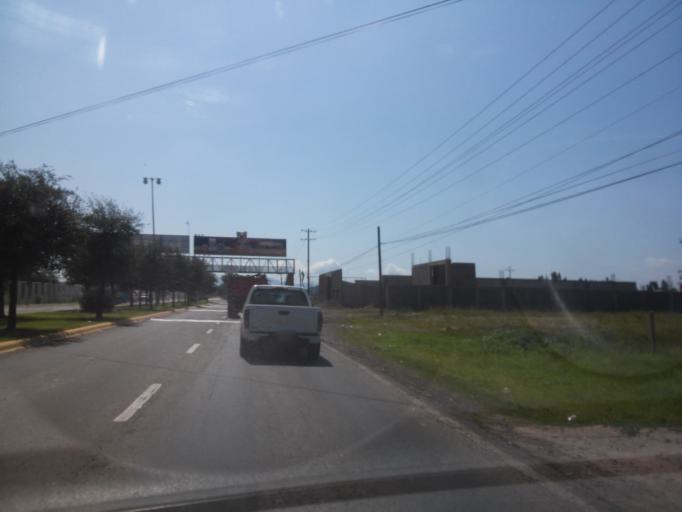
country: MX
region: Durango
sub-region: Durango
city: Sebastian Lerdo de Tejada
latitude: 23.9898
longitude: -104.6195
